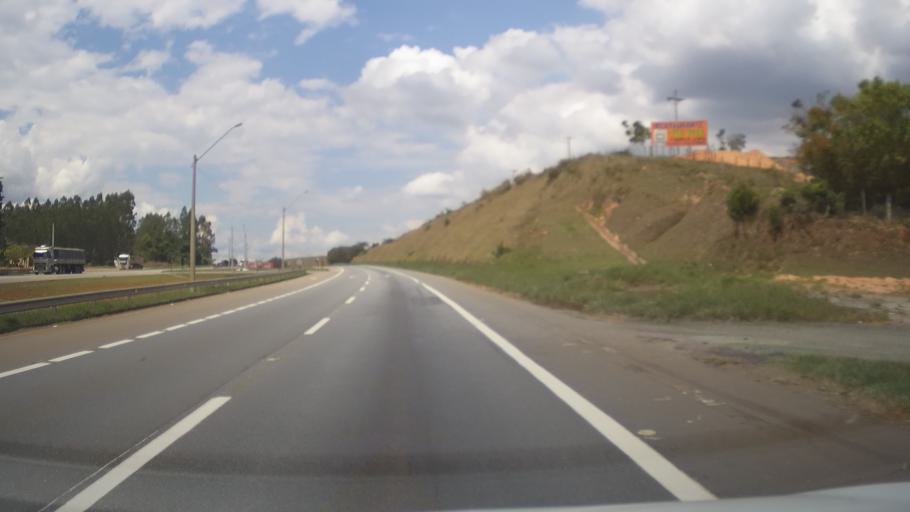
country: BR
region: Minas Gerais
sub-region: Nepomuceno
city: Nepomuceno
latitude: -21.3057
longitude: -45.1573
